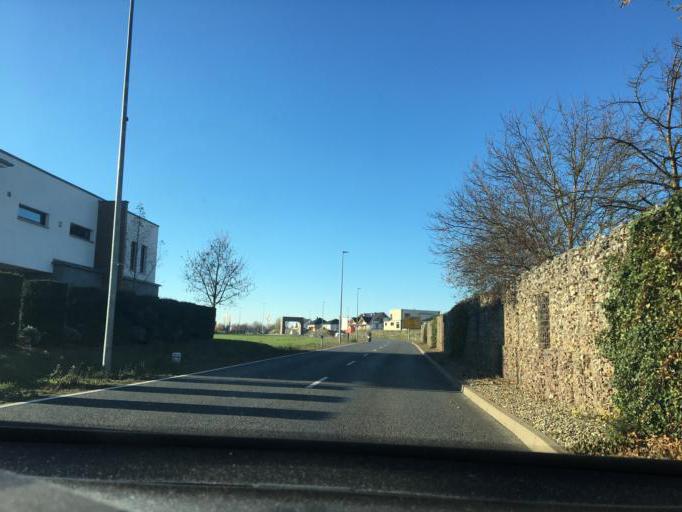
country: DE
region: Hesse
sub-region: Regierungsbezirk Darmstadt
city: Langenselbold
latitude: 50.1801
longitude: 9.0257
